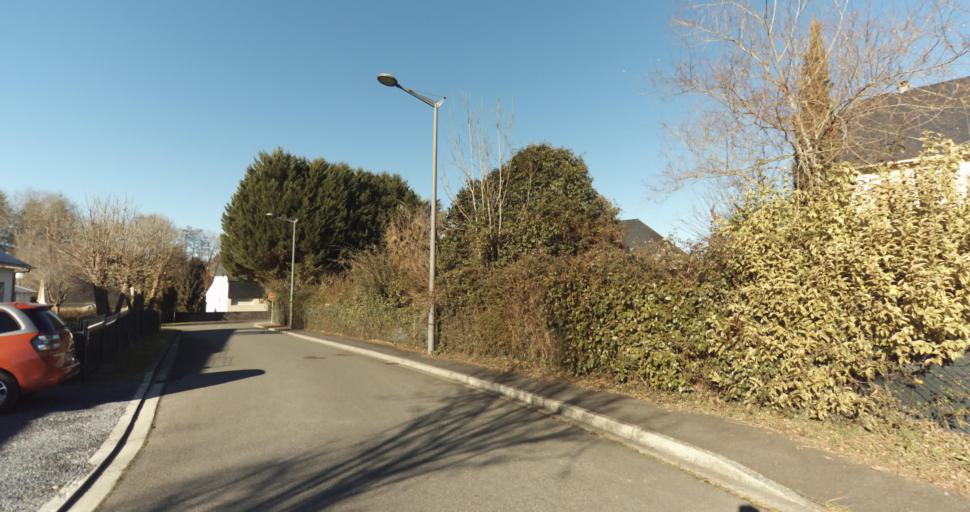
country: FR
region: Aquitaine
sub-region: Departement des Pyrenees-Atlantiques
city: Morlaas
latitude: 43.3441
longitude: -0.2582
